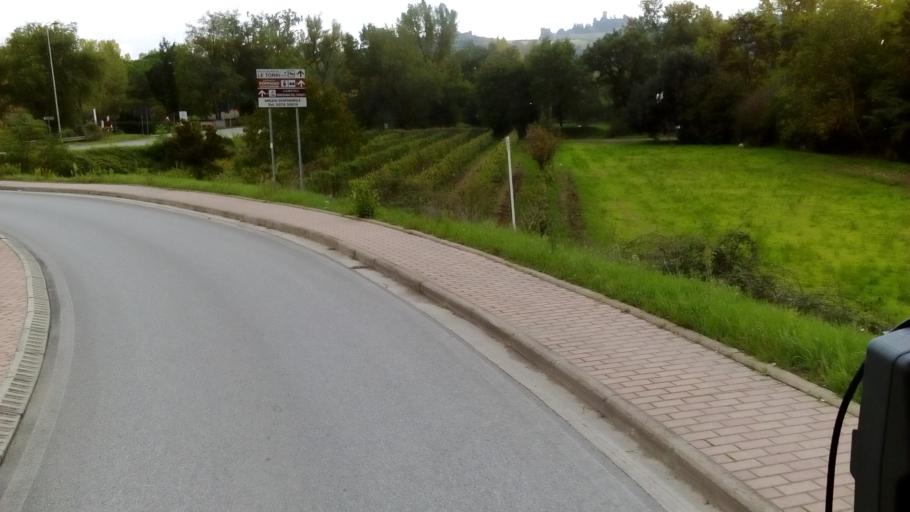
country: IT
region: Tuscany
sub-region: Province of Florence
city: Montespertoli
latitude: 43.6614
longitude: 11.0839
